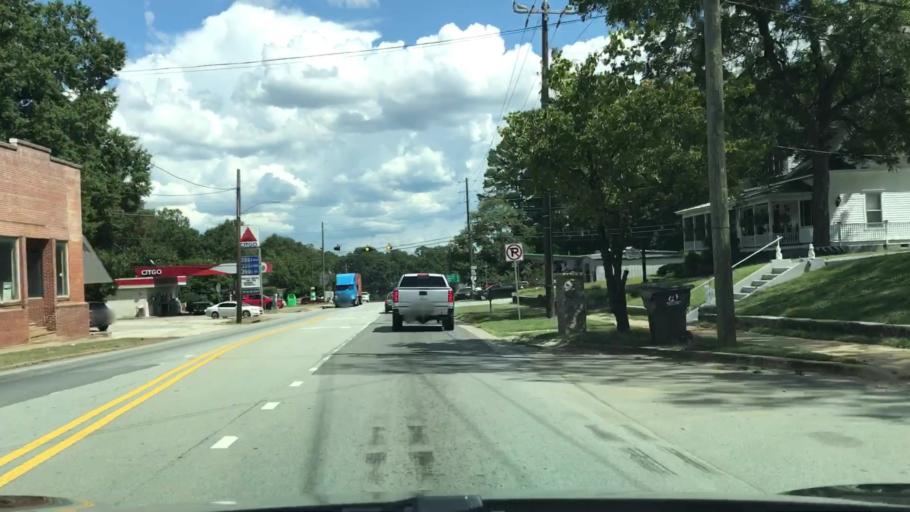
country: US
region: Georgia
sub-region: Greene County
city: Greensboro
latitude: 33.5757
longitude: -83.1805
